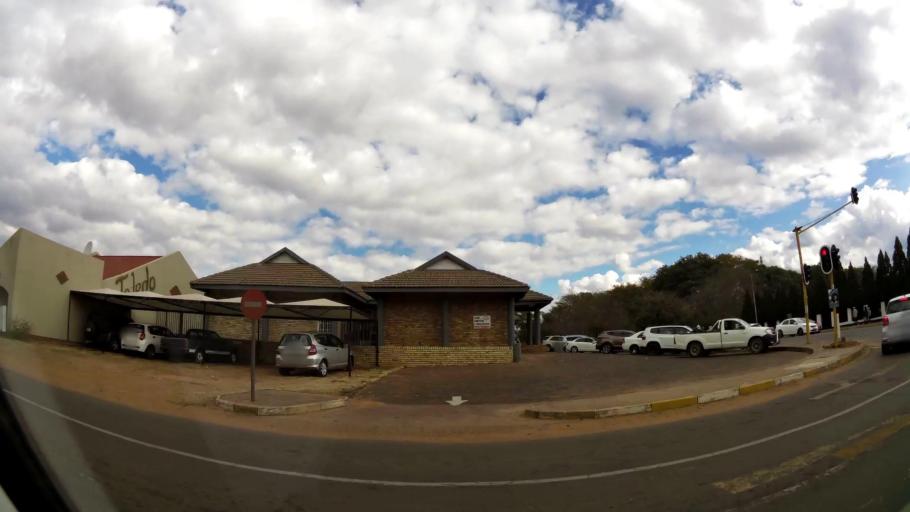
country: ZA
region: Limpopo
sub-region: Waterberg District Municipality
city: Modimolle
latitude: -24.7015
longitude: 28.4044
